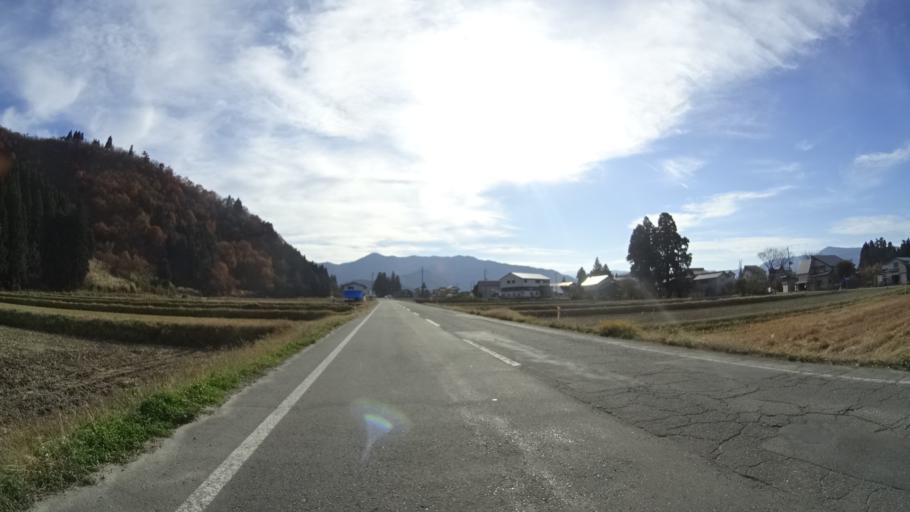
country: JP
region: Niigata
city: Shiozawa
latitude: 37.0270
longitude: 138.8821
